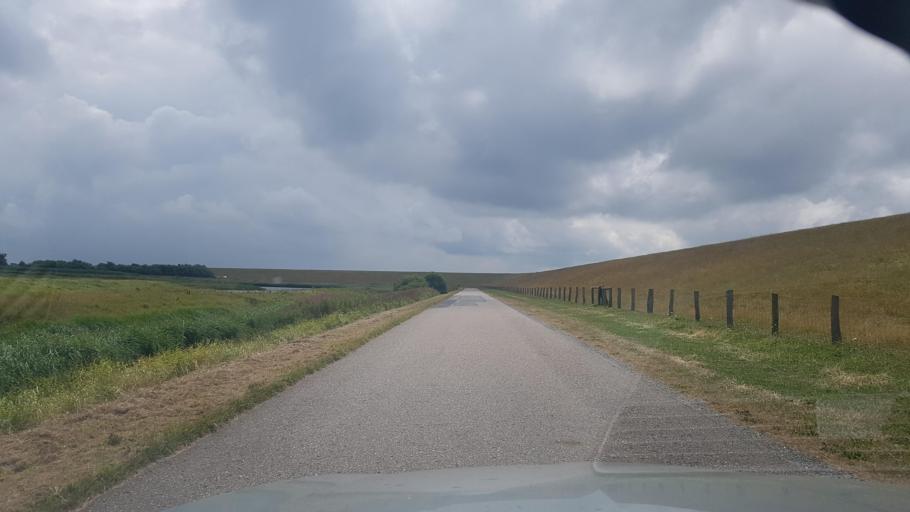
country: DE
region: Schleswig-Holstein
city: Elisabeth-Sophien-Koog
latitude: 54.4935
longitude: 8.8088
